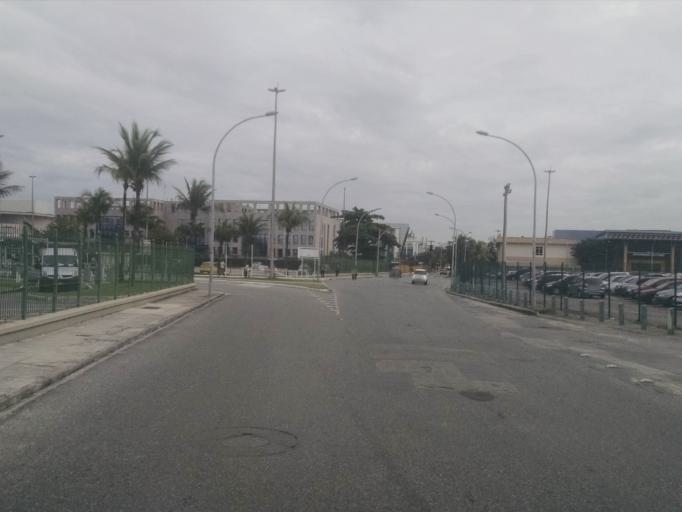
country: BR
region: Rio de Janeiro
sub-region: Rio De Janeiro
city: Rio de Janeiro
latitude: -22.9954
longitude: -43.3602
